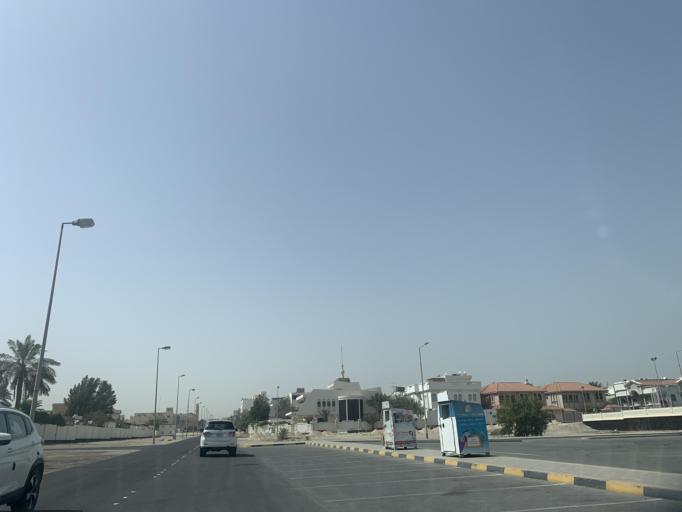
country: BH
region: Northern
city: Madinat `Isa
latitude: 26.1531
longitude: 50.5288
